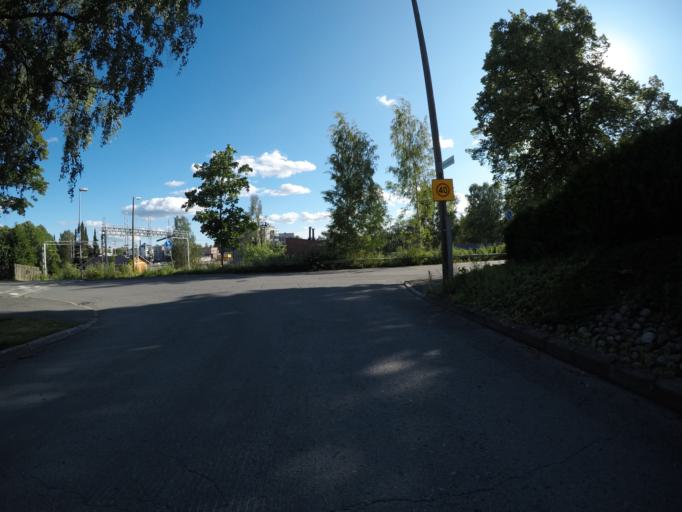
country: FI
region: Haeme
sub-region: Haemeenlinna
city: Haemeenlinna
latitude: 61.0042
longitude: 24.4758
